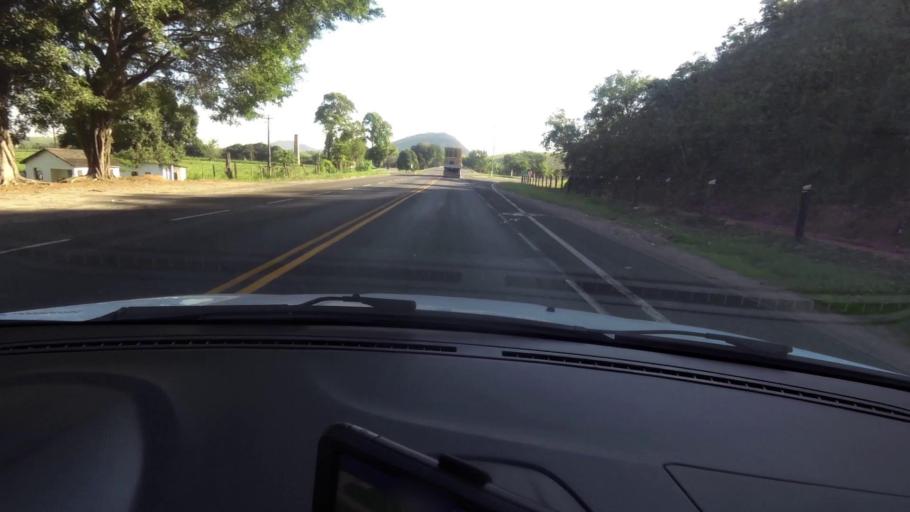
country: BR
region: Espirito Santo
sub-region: Alfredo Chaves
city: Alfredo Chaves
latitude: -20.6855
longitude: -40.6739
